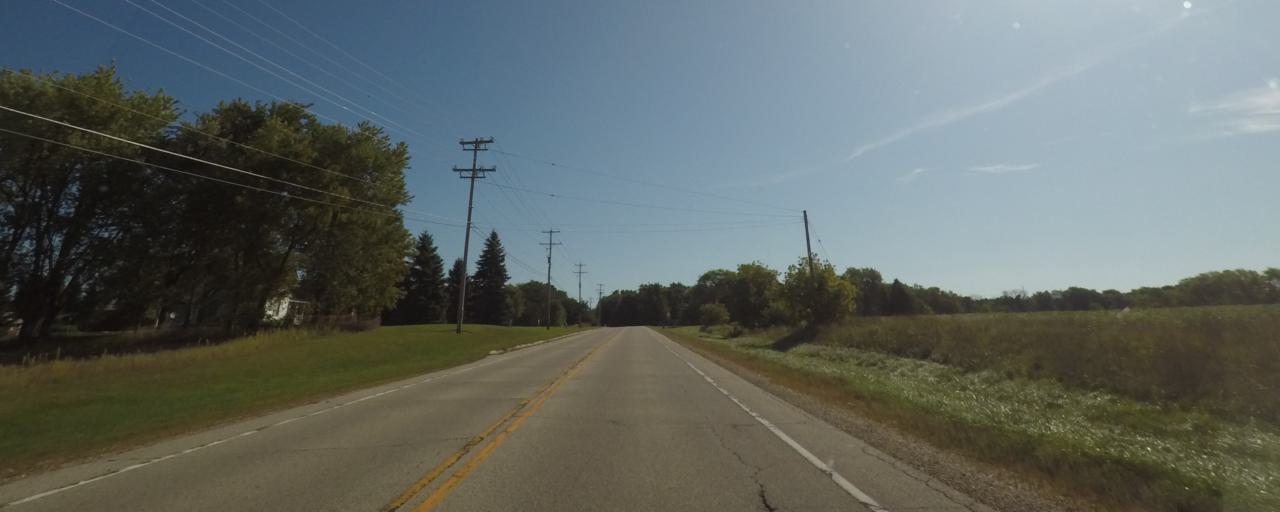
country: US
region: Wisconsin
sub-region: Waukesha County
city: Dousman
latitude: 43.0214
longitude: -88.4906
